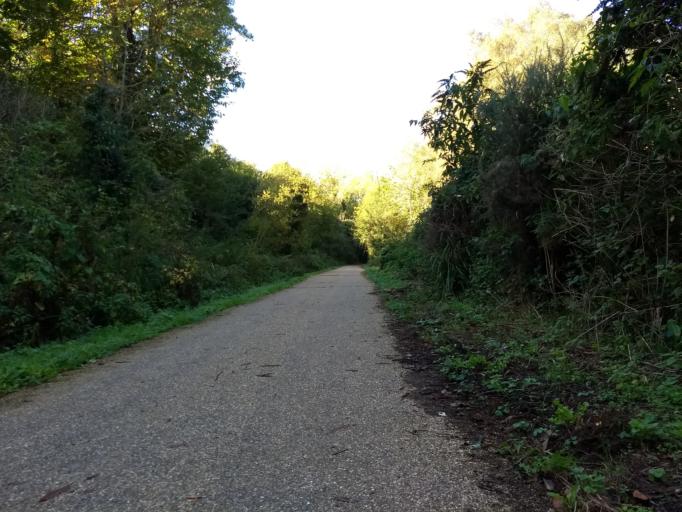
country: GB
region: England
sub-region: Isle of Wight
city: Shanklin
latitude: 50.6302
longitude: -1.1949
